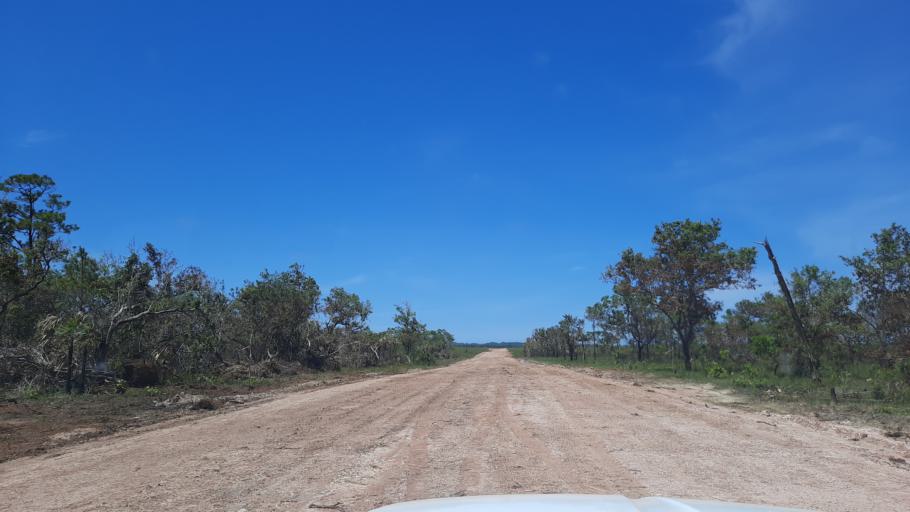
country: BZ
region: Belize
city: Belize City
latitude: 17.2517
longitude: -88.4233
